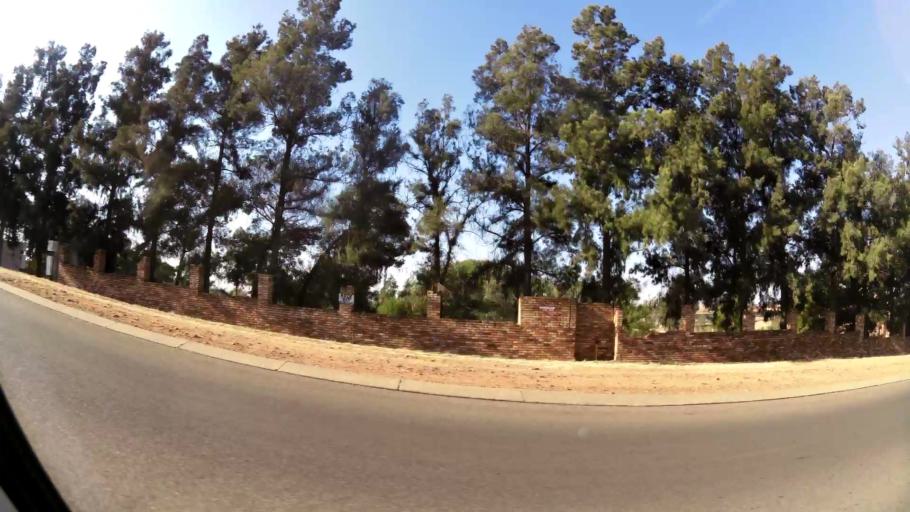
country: ZA
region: Gauteng
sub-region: City of Tshwane Metropolitan Municipality
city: Centurion
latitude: -25.8349
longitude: 28.3006
